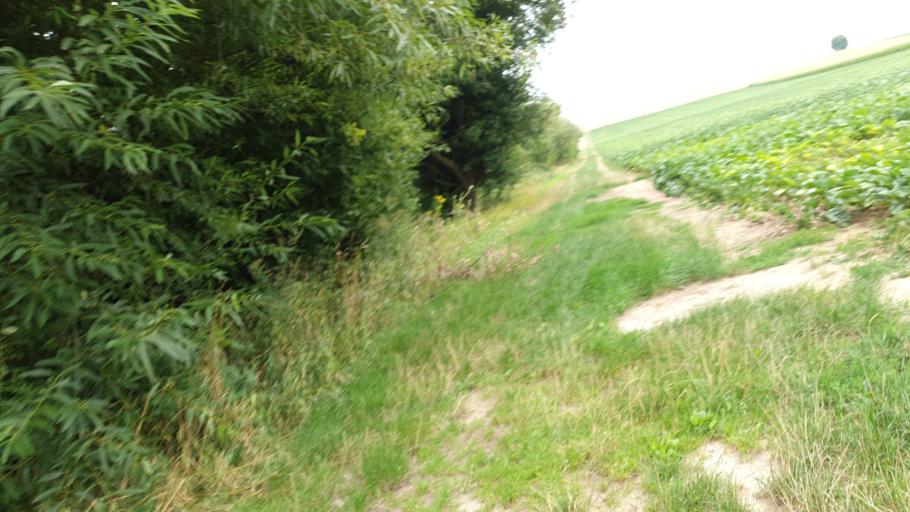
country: DE
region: Rheinland-Pfalz
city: Oberhausen
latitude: 49.1147
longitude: 8.0581
